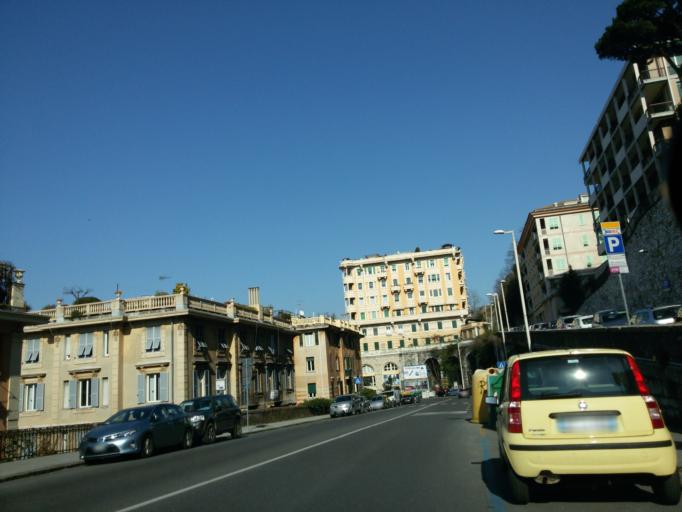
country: IT
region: Liguria
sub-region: Provincia di Genova
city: Genoa
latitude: 44.4024
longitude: 8.9558
